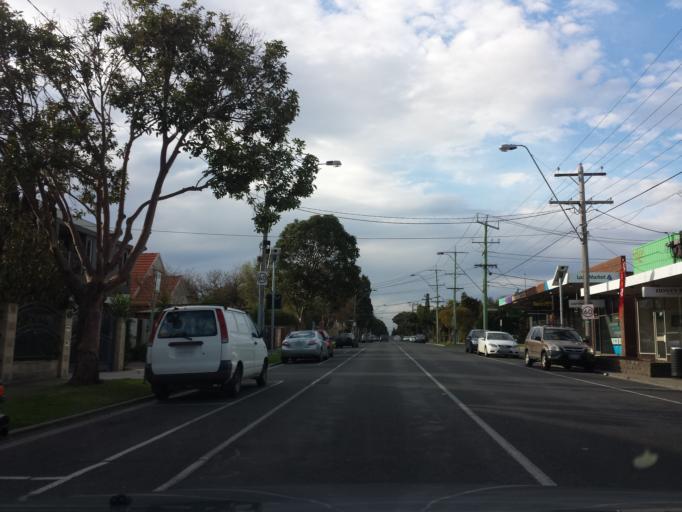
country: AU
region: Victoria
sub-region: Bayside
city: Cheltenham
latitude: -37.9793
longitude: 145.0531
